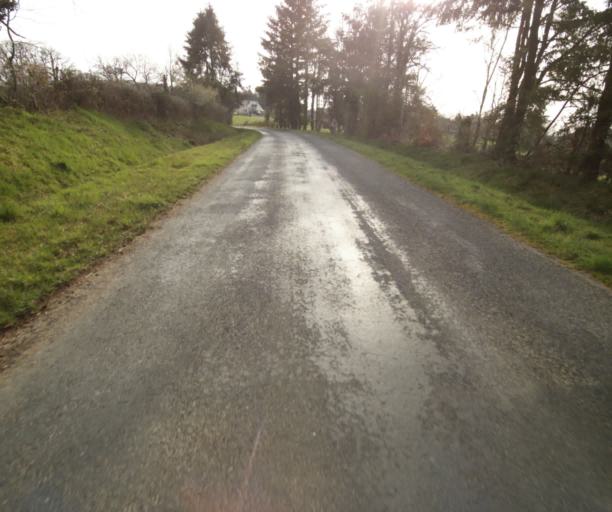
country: FR
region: Limousin
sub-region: Departement de la Correze
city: Chamboulive
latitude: 45.4385
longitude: 1.7788
